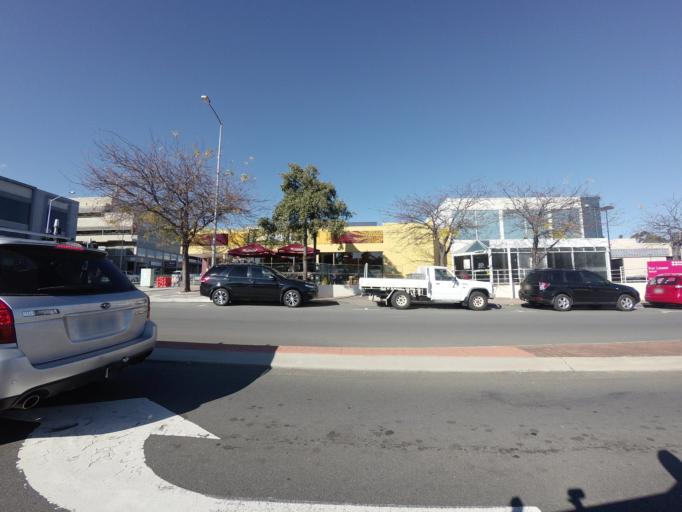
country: AU
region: Tasmania
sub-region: Clarence
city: Bellerive
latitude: -42.8665
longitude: 147.3691
